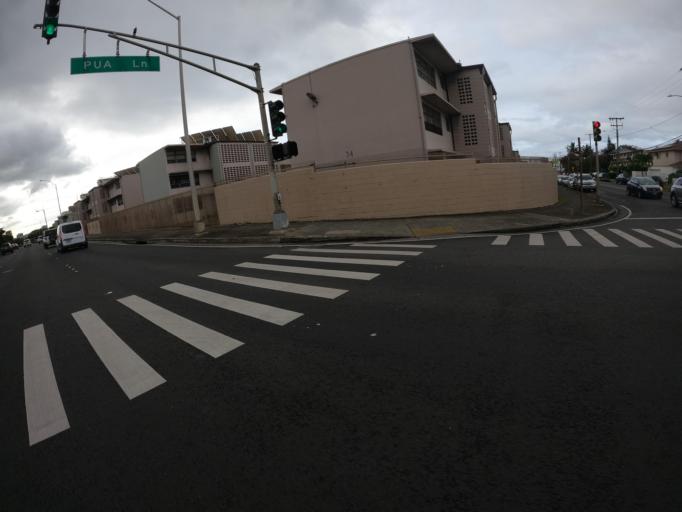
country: US
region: Hawaii
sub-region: Honolulu County
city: Honolulu
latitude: 21.3217
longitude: -157.8635
